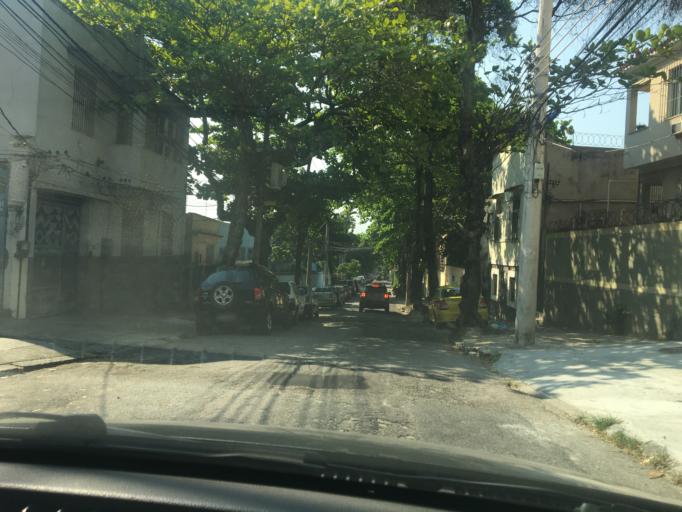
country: BR
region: Rio de Janeiro
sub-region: Rio De Janeiro
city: Rio de Janeiro
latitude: -22.8968
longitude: -43.2255
